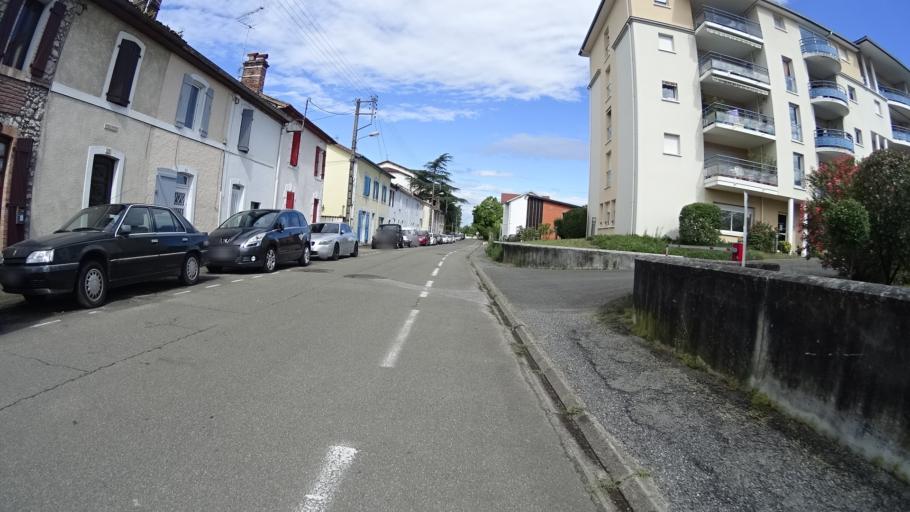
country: FR
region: Aquitaine
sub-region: Departement des Landes
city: Dax
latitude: 43.7027
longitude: -1.0599
